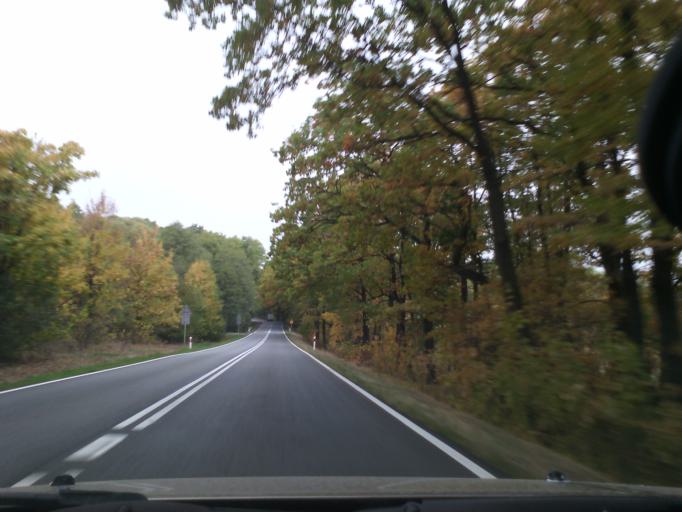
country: PL
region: Lower Silesian Voivodeship
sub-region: Powiat swidnicki
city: Swiebodzice
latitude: 50.8756
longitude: 16.2837
